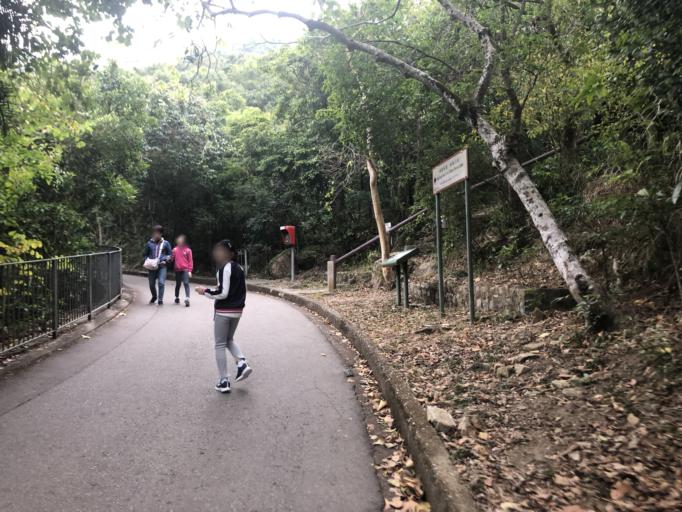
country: HK
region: Wanchai
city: Wan Chai
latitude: 22.2789
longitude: 114.2098
